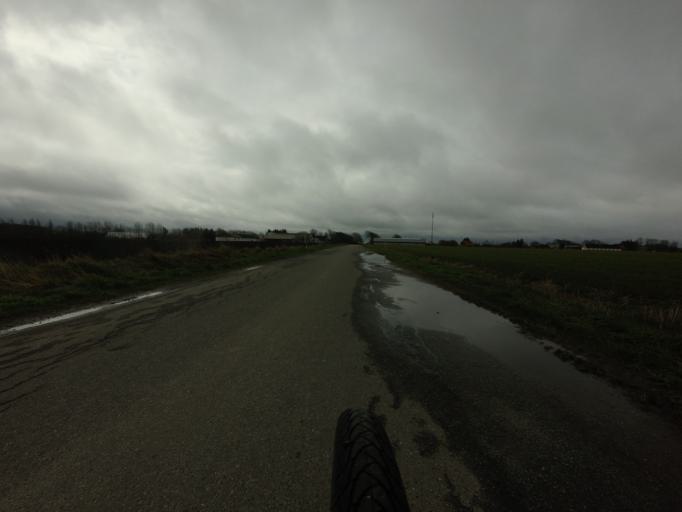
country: DK
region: North Denmark
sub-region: Hjorring Kommune
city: Vra
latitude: 57.3695
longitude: 9.8376
